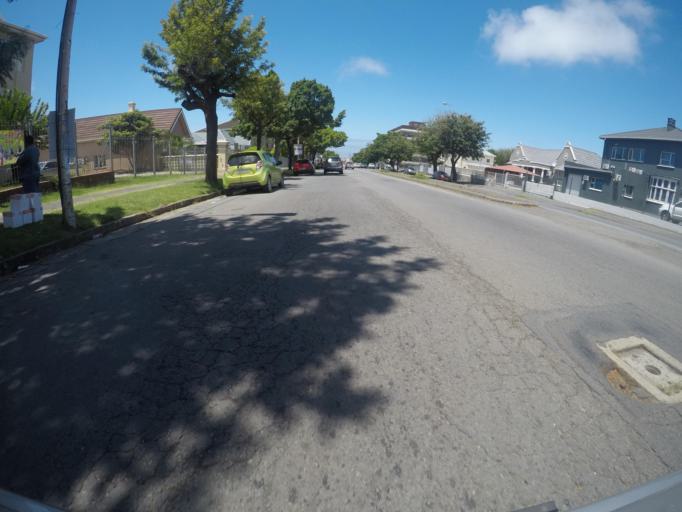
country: ZA
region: Eastern Cape
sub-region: Buffalo City Metropolitan Municipality
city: East London
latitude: -33.0008
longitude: 27.8989
